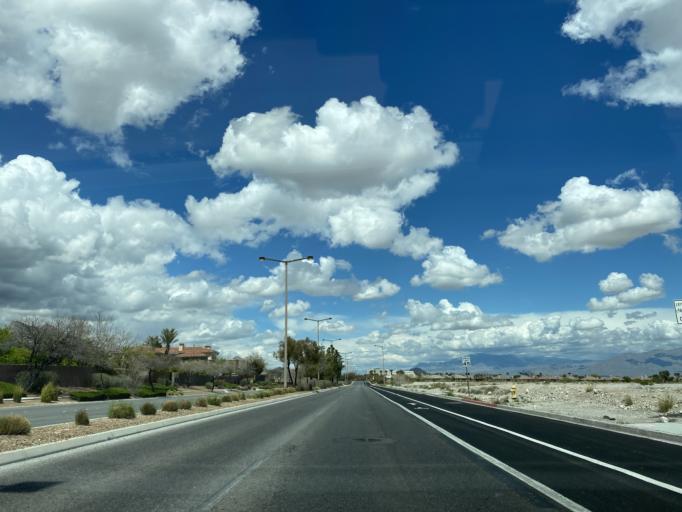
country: US
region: Nevada
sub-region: Clark County
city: Summerlin South
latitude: 36.1689
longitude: -115.3153
